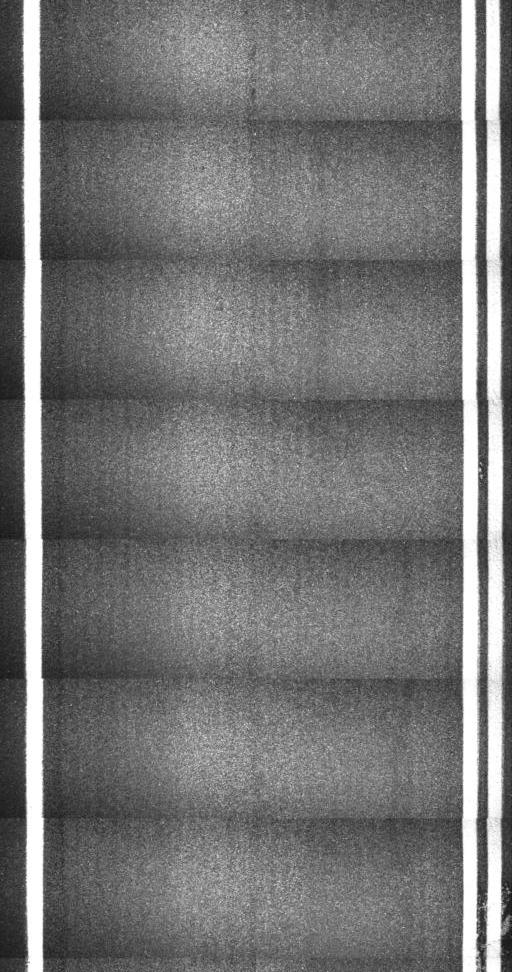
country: US
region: Vermont
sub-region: Windham County
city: Dover
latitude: 42.9957
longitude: -72.8877
